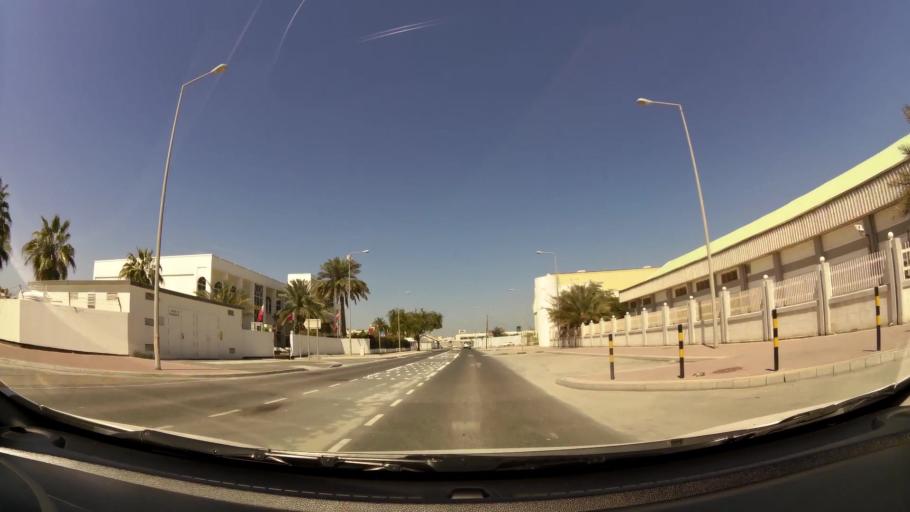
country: BH
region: Muharraq
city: Al Muharraq
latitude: 26.2719
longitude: 50.6144
